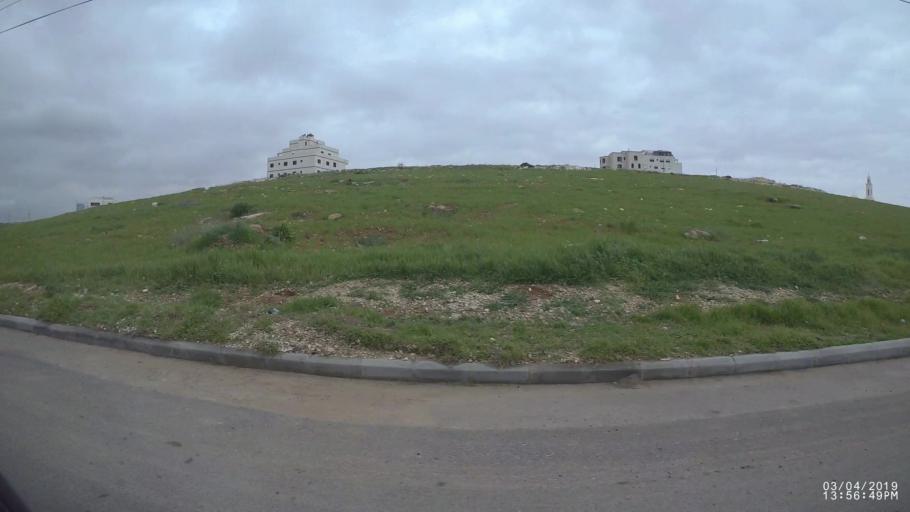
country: JO
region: Amman
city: Wadi as Sir
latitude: 31.9334
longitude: 35.8477
